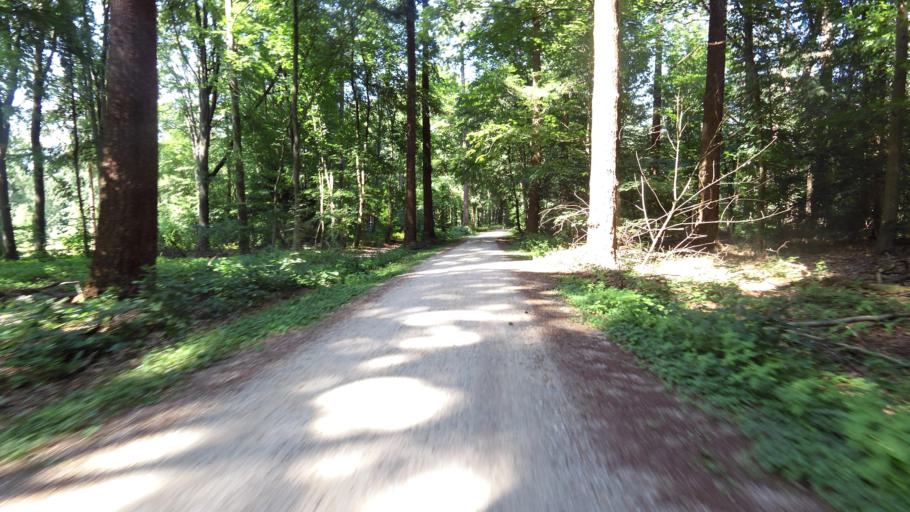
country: NL
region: Gelderland
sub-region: Gemeente Arnhem
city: Hoogkamp
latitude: 52.0101
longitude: 5.8691
